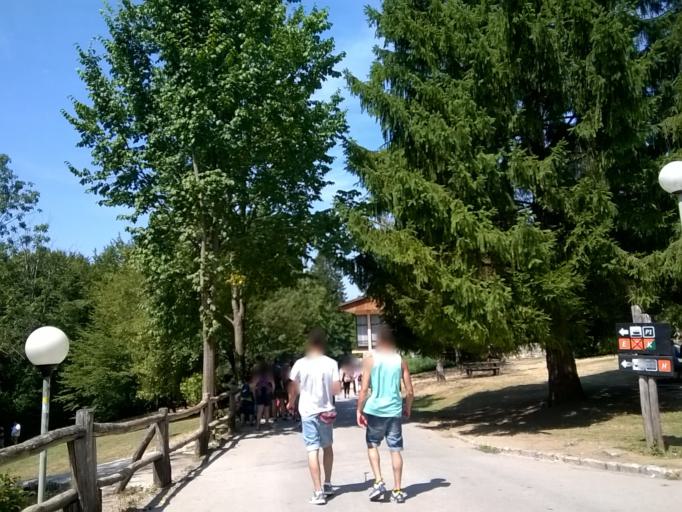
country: HR
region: Licko-Senjska
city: Jezerce
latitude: 44.8819
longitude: 15.6188
